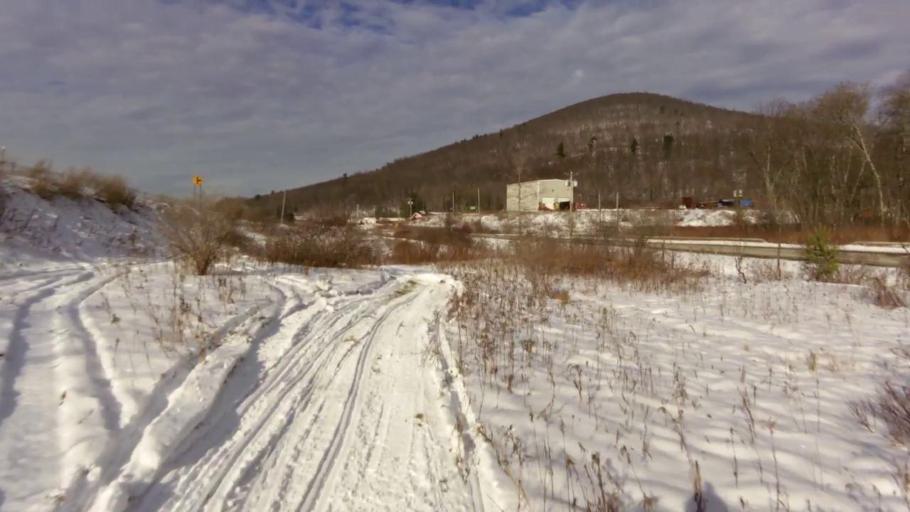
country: US
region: Pennsylvania
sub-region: McKean County
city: Foster Brook
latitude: 42.0010
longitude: -78.6186
